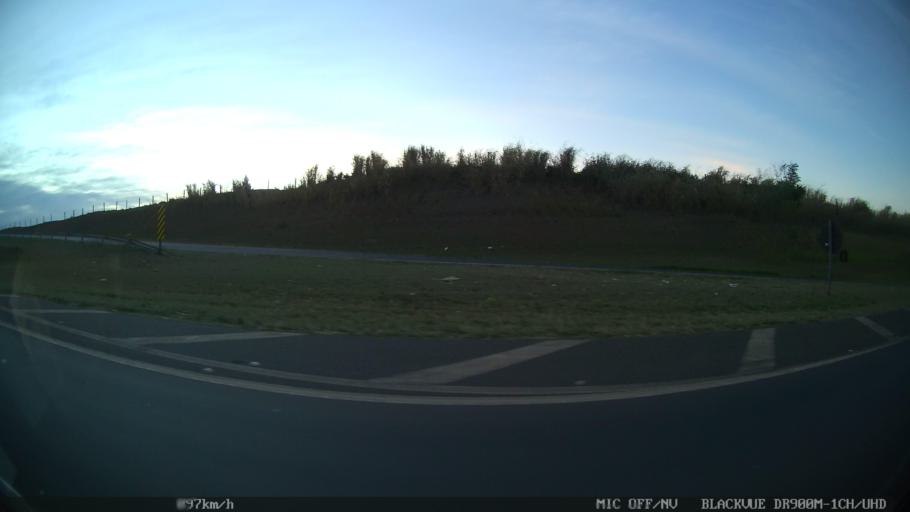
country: BR
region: Sao Paulo
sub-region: Catanduva
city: Catanduva
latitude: -21.1144
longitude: -48.9755
